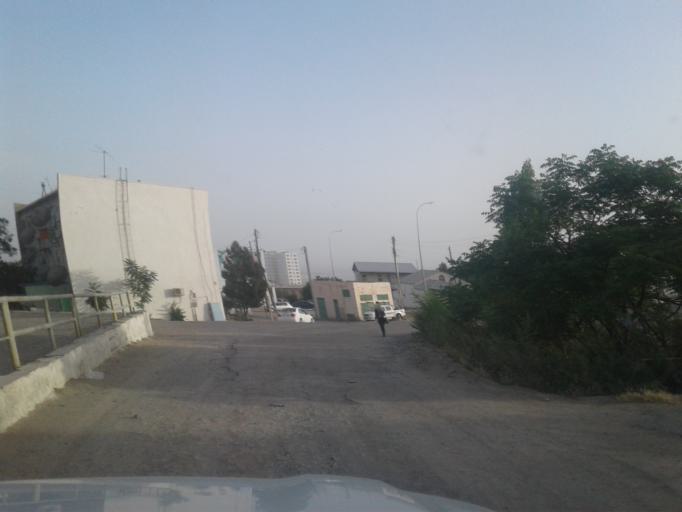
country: TM
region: Balkan
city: Turkmenbasy
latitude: 40.0058
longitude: 52.9651
